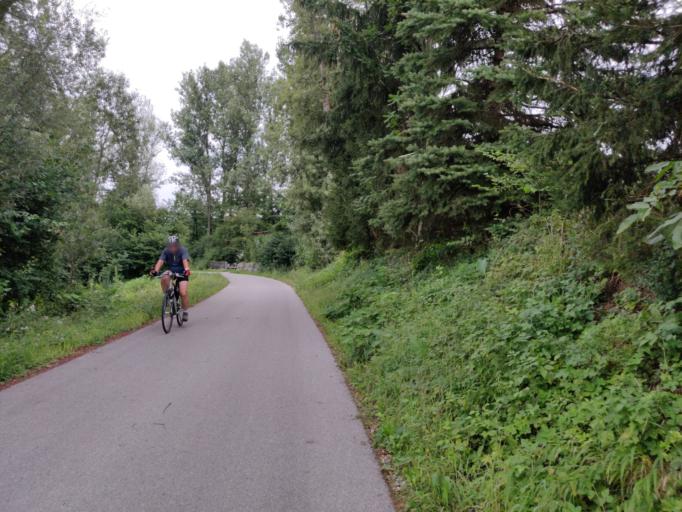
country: AT
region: Lower Austria
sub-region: Politischer Bezirk Melk
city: Ybbs an der Donau
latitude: 48.1794
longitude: 15.1211
